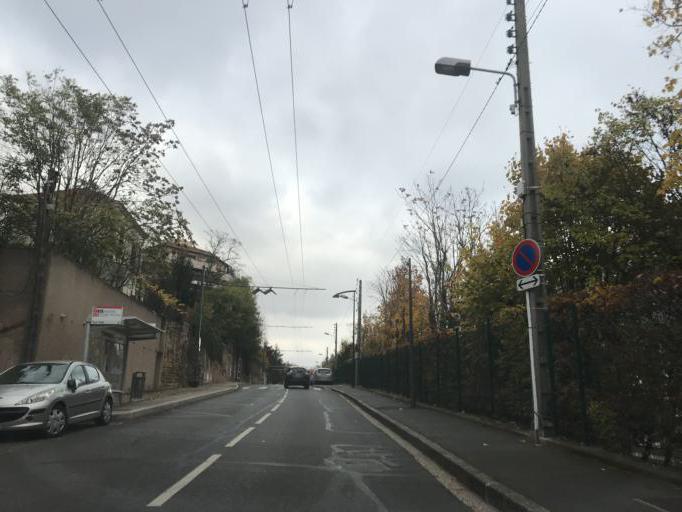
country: FR
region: Rhone-Alpes
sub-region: Departement du Rhone
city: Caluire-et-Cuire
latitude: 45.7871
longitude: 4.8417
